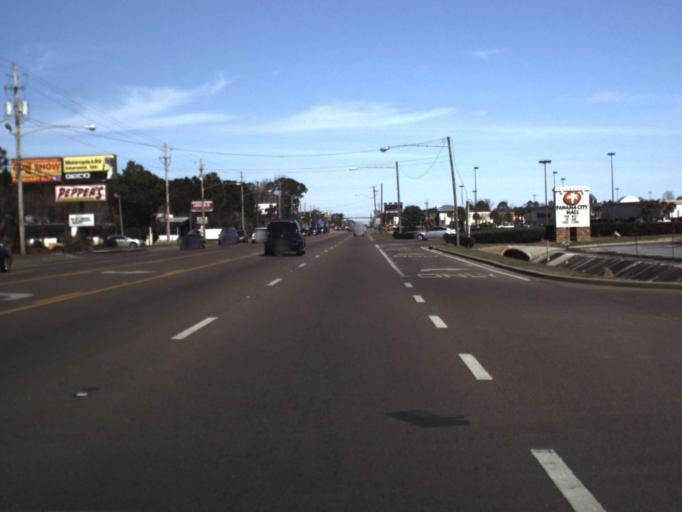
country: US
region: Florida
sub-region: Bay County
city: Panama City
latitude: 30.1848
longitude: -85.6500
